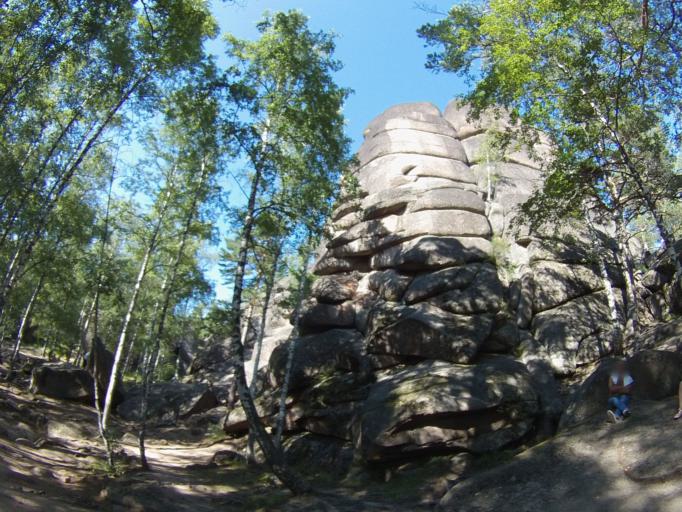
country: RU
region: Krasnoyarskiy
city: Ovsyanka
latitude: 55.9156
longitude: 92.7335
